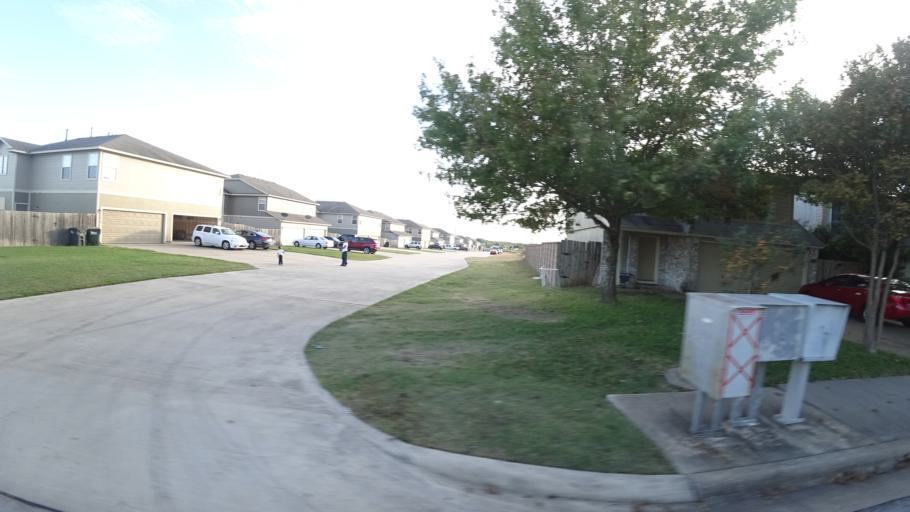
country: US
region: Texas
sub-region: Travis County
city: Pflugerville
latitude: 30.4134
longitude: -97.6468
